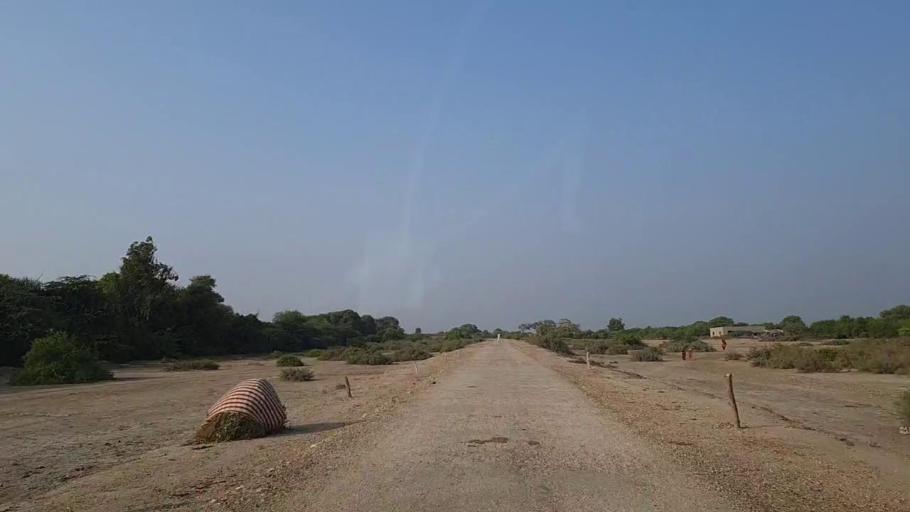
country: PK
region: Sindh
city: Mirpur Sakro
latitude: 24.6437
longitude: 67.7676
